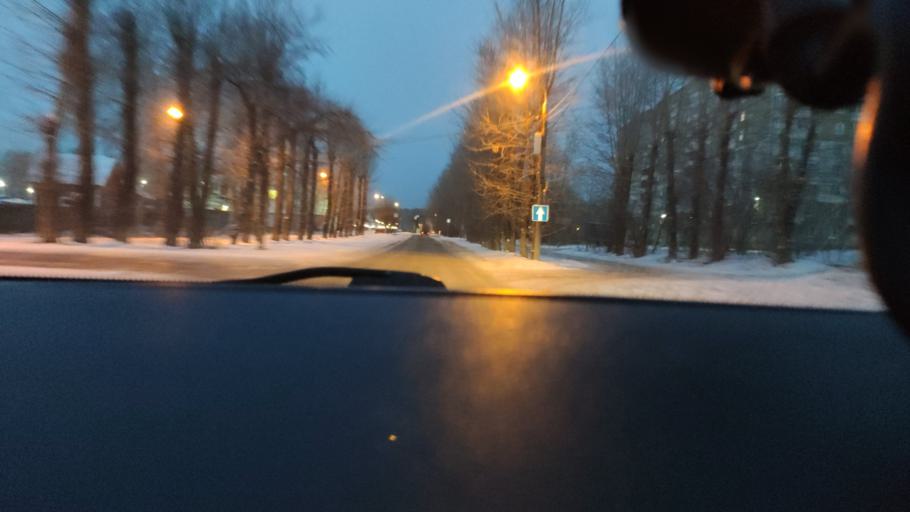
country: RU
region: Perm
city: Overyata
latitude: 58.0123
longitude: 55.9589
